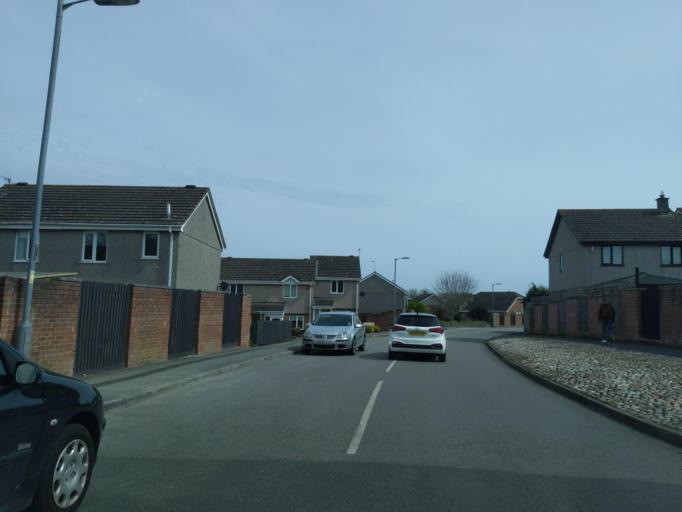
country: GB
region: England
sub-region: Cornwall
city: Torpoint
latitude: 50.3791
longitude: -4.2148
